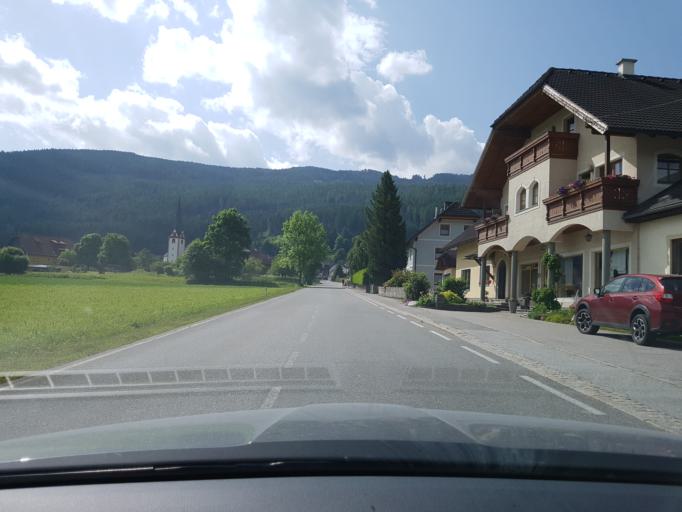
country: AT
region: Salzburg
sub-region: Politischer Bezirk Tamsweg
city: Sankt Margarethen im Lungau
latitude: 47.0815
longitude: 13.6924
